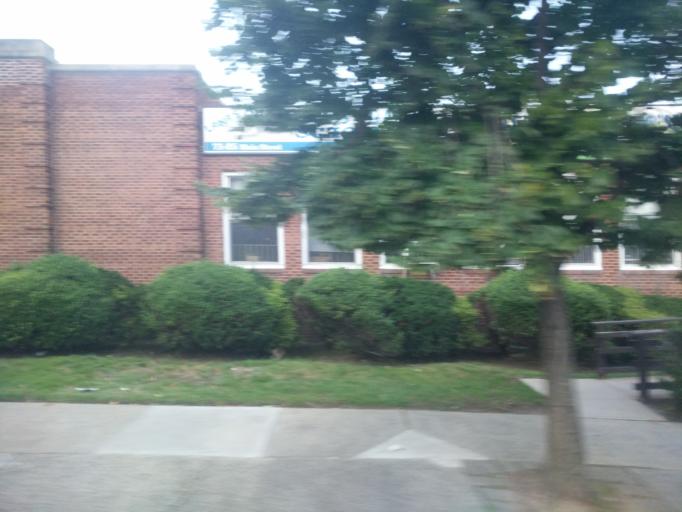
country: US
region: New York
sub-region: Queens County
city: Jamaica
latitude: 40.7271
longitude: -73.8219
